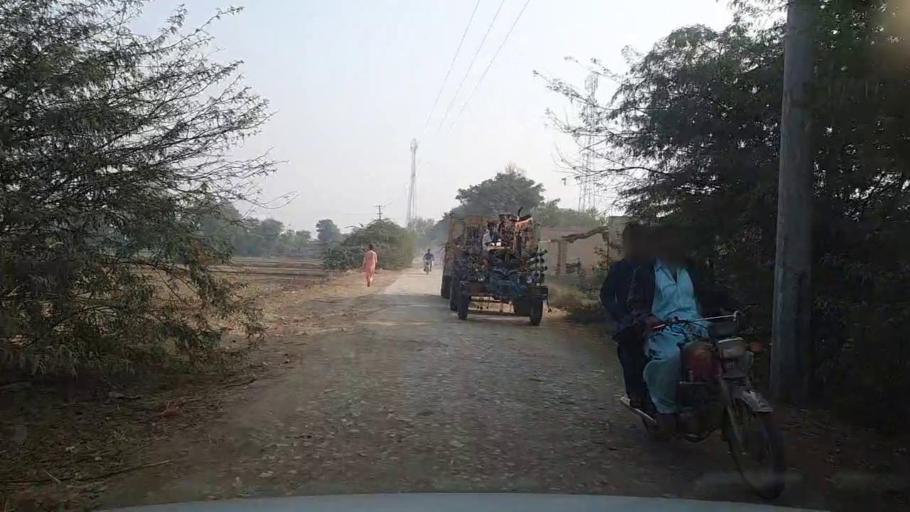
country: PK
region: Sindh
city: Kandiari
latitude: 27.0318
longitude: 68.4863
